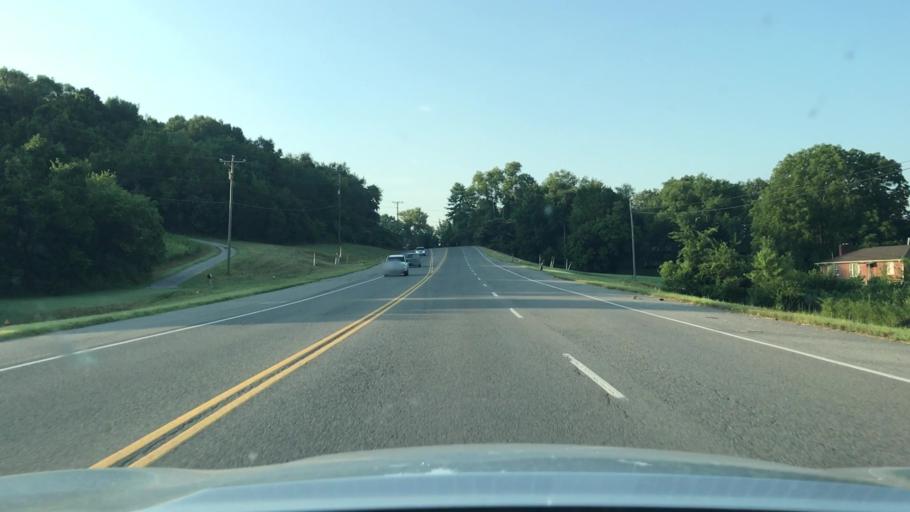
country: US
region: Tennessee
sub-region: Williamson County
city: Nolensville
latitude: 36.0073
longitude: -86.7007
